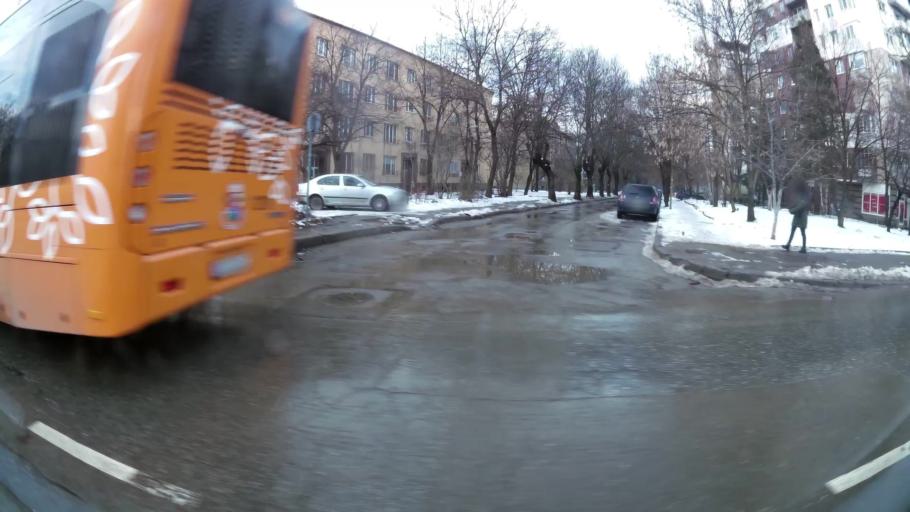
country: BG
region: Sofia-Capital
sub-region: Stolichna Obshtina
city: Sofia
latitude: 42.7042
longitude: 23.2853
